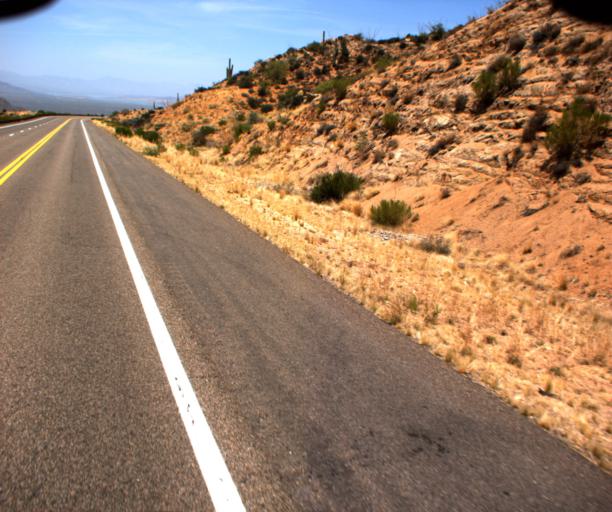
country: US
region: Arizona
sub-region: Gila County
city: Miami
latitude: 33.5472
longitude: -110.9437
